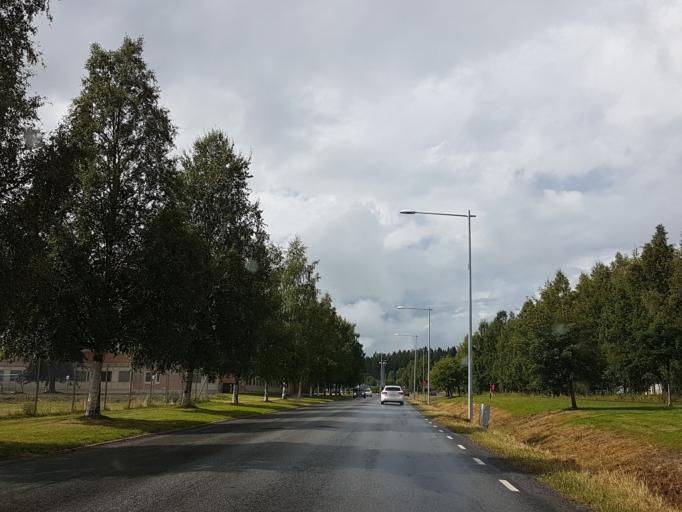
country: SE
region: Vaesterbotten
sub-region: Umea Kommun
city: Ersmark
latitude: 63.8526
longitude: 20.3066
